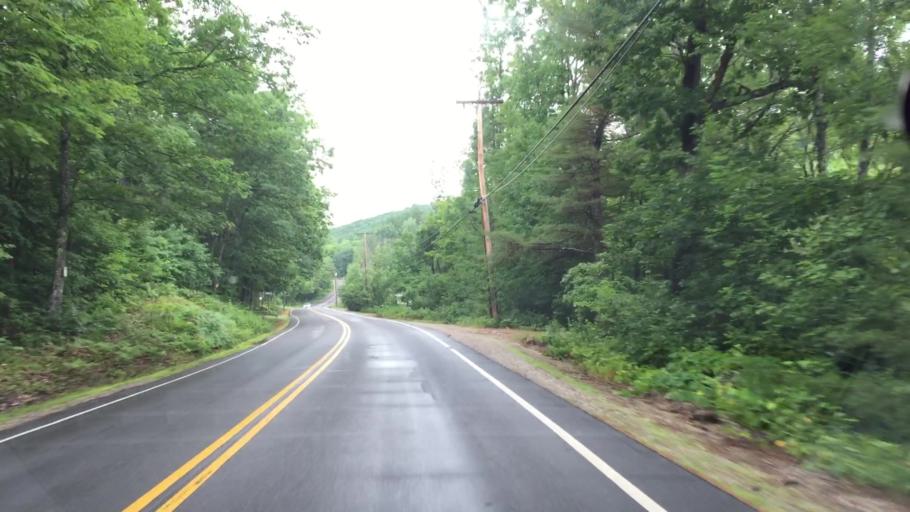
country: US
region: New Hampshire
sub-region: Carroll County
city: Center Harbor
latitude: 43.7418
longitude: -71.4779
